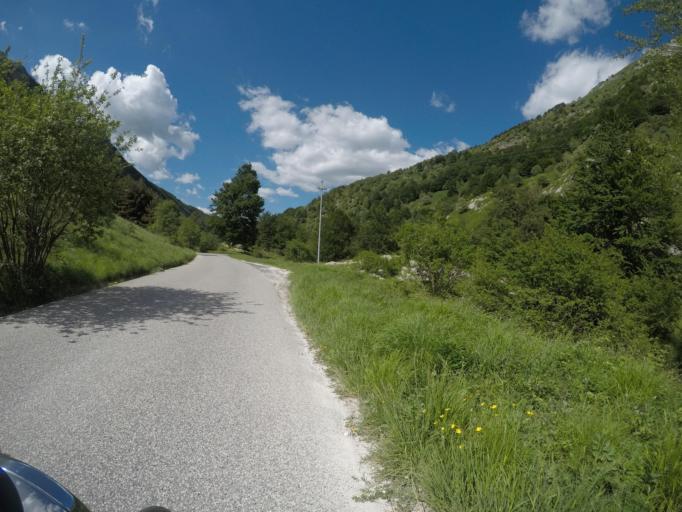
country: IT
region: Tuscany
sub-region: Provincia di Lucca
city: Minucciano
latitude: 44.1374
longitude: 10.1965
